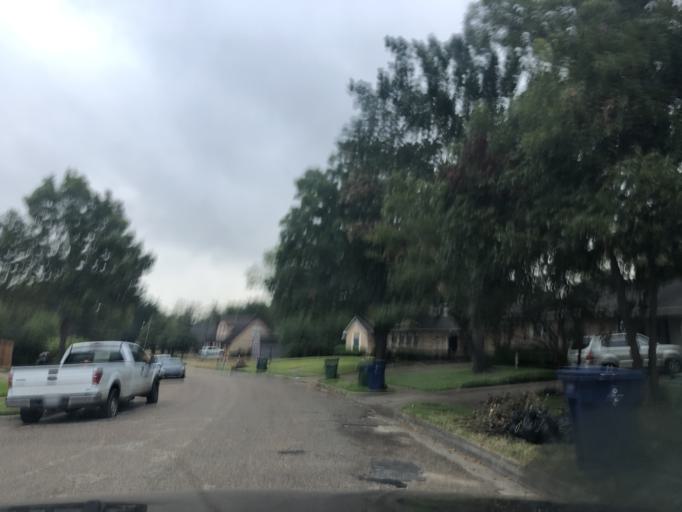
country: US
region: Texas
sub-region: Dallas County
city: Garland
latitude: 32.8719
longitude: -96.6457
